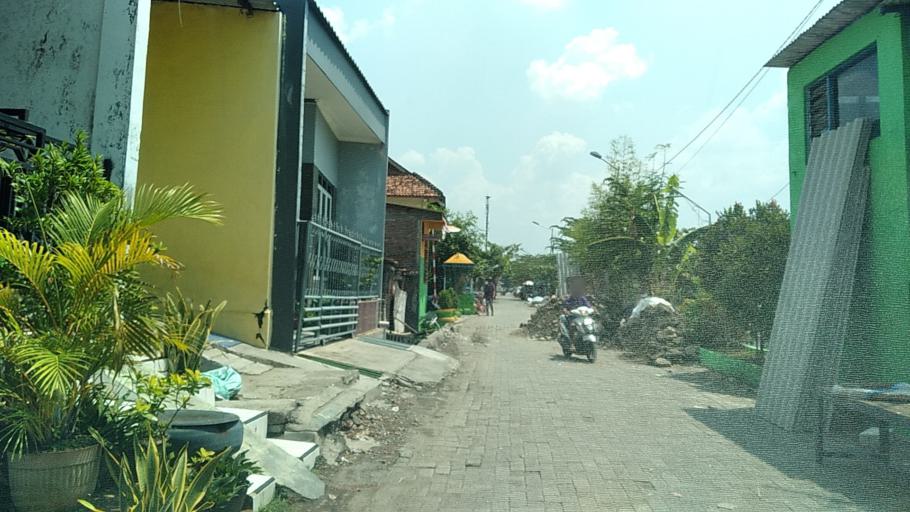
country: ID
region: Central Java
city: Semarang
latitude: -6.9642
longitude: 110.4408
